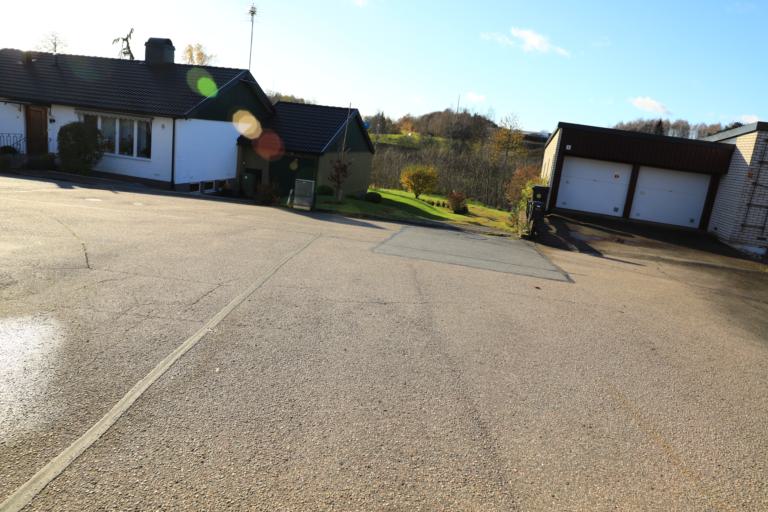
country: SE
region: Vaestra Goetaland
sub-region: Marks Kommun
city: Kinna
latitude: 57.5001
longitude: 12.6743
